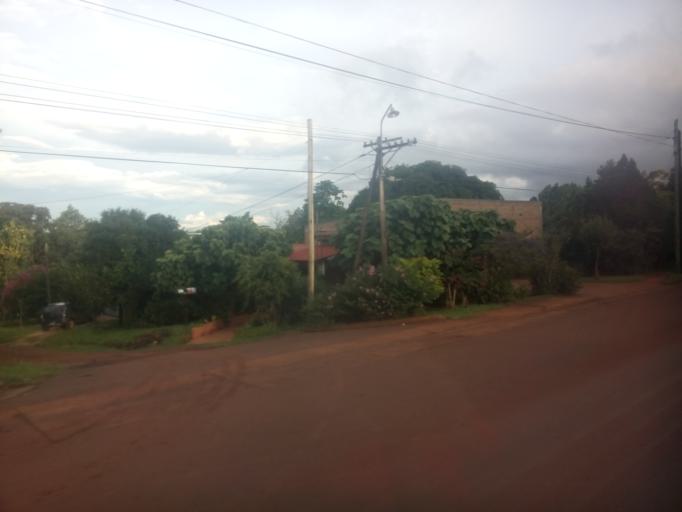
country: AR
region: Misiones
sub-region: Departamento de Obera
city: Obera
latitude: -27.4949
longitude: -55.1438
